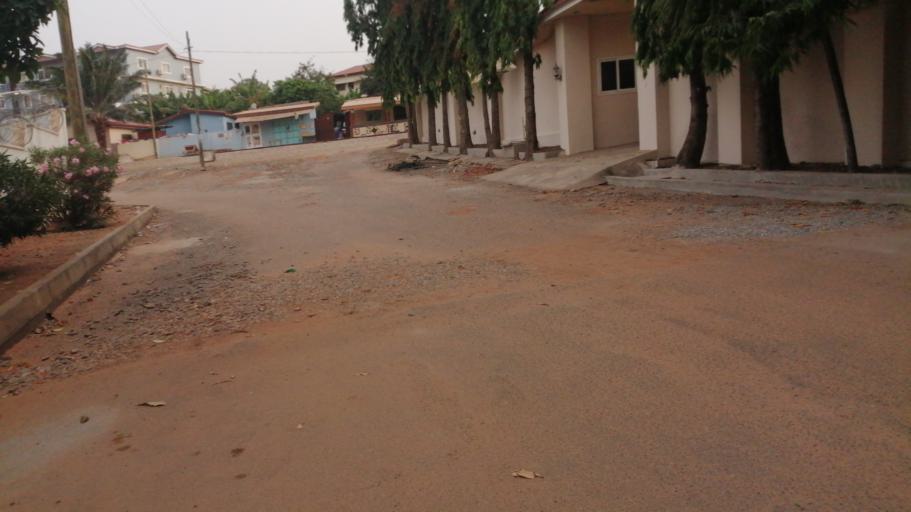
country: GH
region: Greater Accra
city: Medina Estates
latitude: 5.6187
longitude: -0.1794
